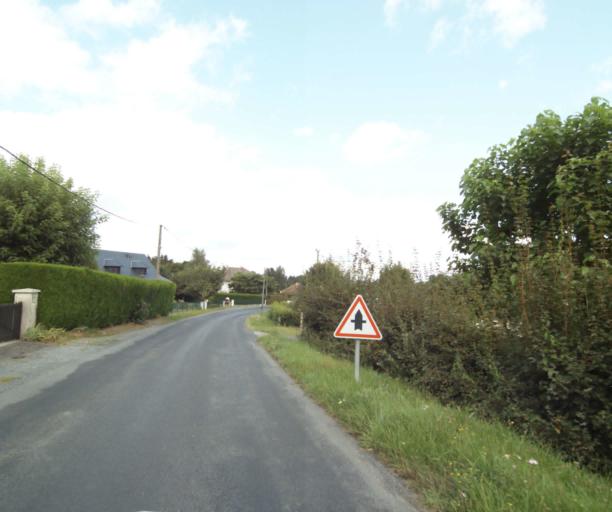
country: FR
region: Limousin
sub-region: Departement de la Correze
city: Sainte-Fortunade
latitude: 45.1973
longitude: 1.8197
